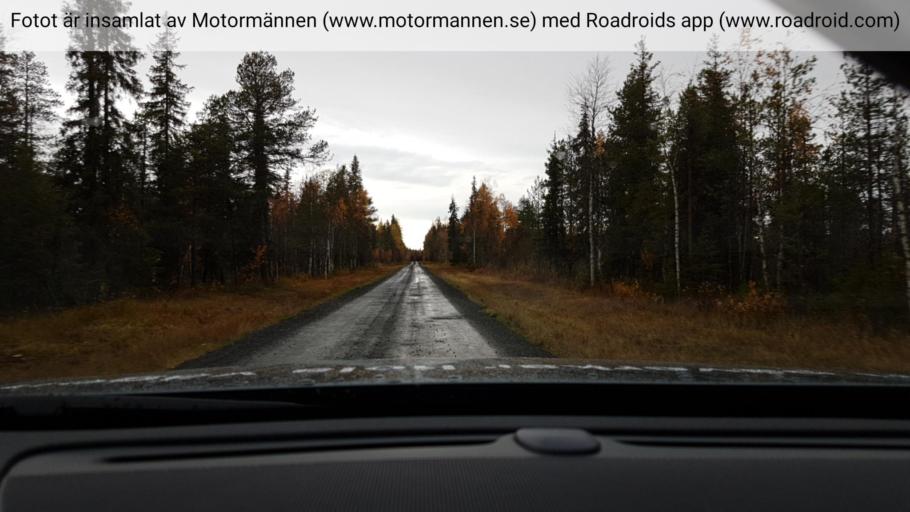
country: SE
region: Norrbotten
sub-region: Pajala Kommun
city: Pajala
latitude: 67.0882
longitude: 22.7598
